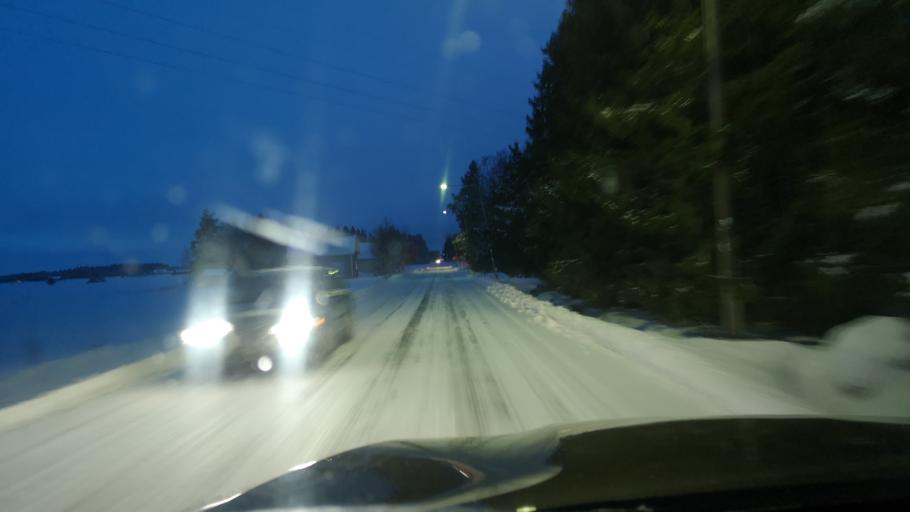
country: FI
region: Varsinais-Suomi
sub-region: Loimaa
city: Loimaa
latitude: 60.8727
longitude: 23.0900
